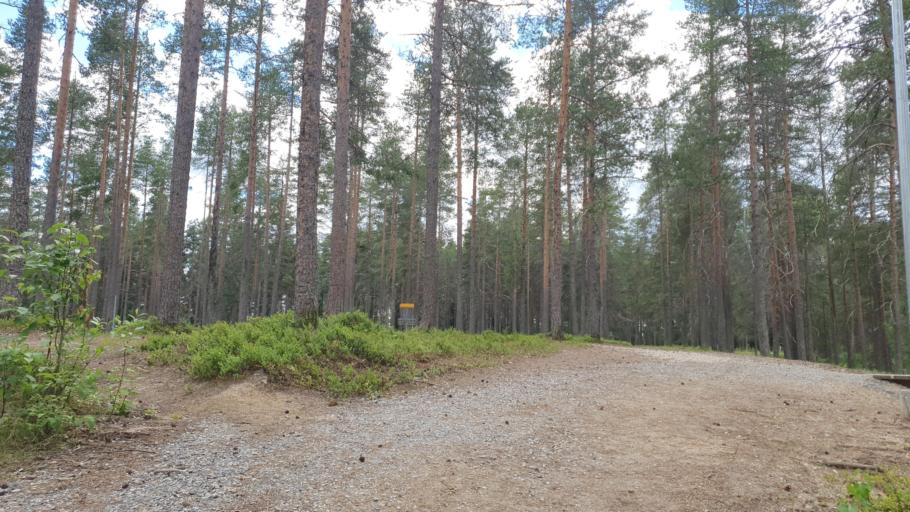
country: FI
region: Kainuu
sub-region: Kehys-Kainuu
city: Kuhmo
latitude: 64.1312
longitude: 29.5374
